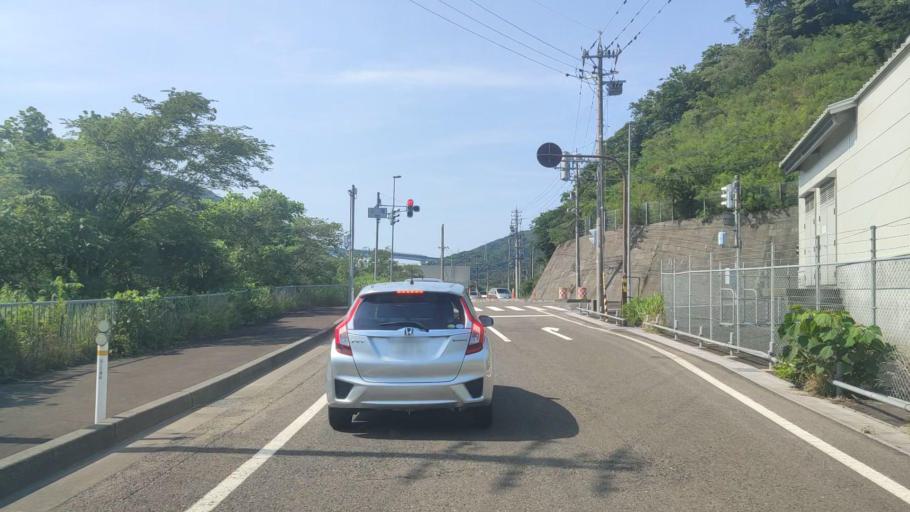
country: JP
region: Fukui
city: Tsuruga
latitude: 35.6149
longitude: 136.0836
